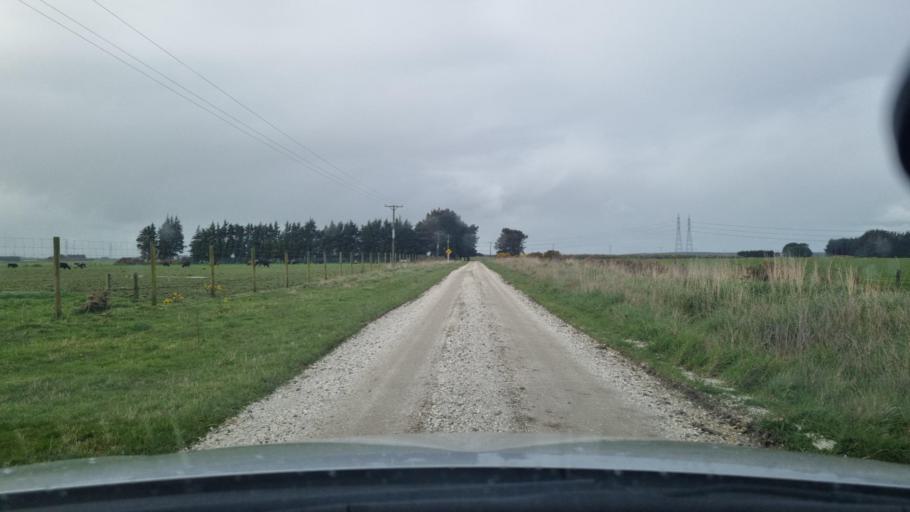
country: NZ
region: Southland
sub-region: Invercargill City
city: Invercargill
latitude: -46.4933
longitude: 168.4255
